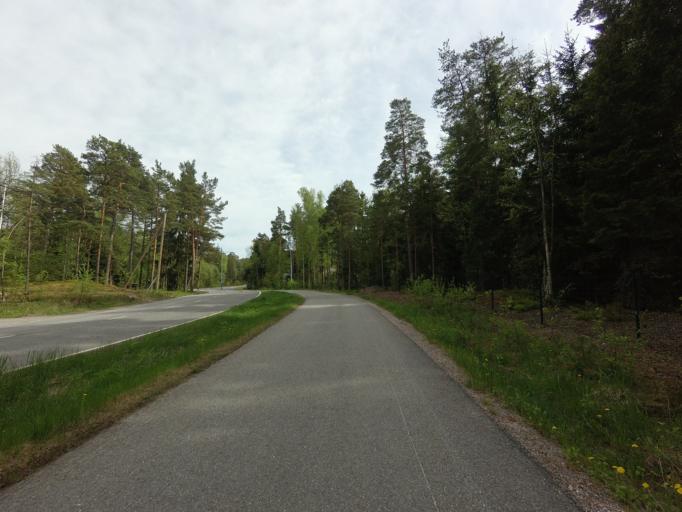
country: FI
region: Uusimaa
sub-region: Helsinki
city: Koukkuniemi
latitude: 60.1253
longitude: 24.7128
